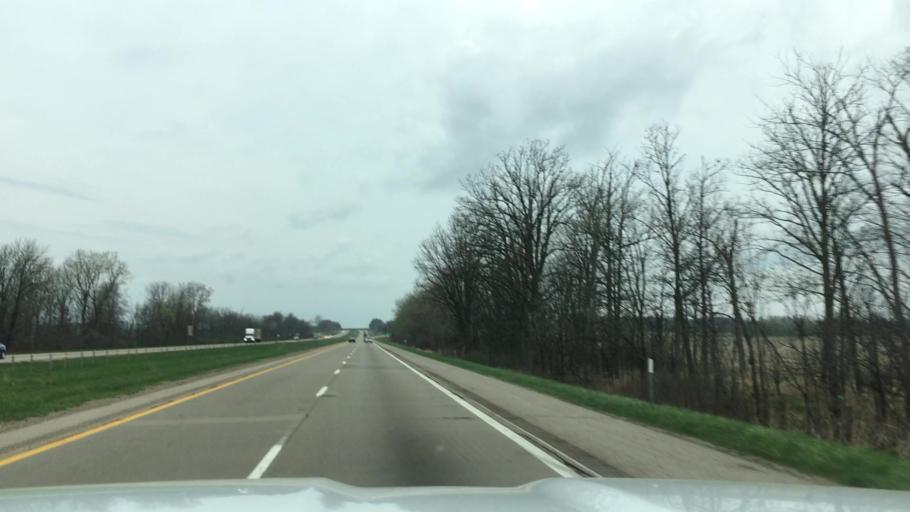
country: US
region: Michigan
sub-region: Ionia County
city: Saranac
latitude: 42.8796
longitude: -85.2274
